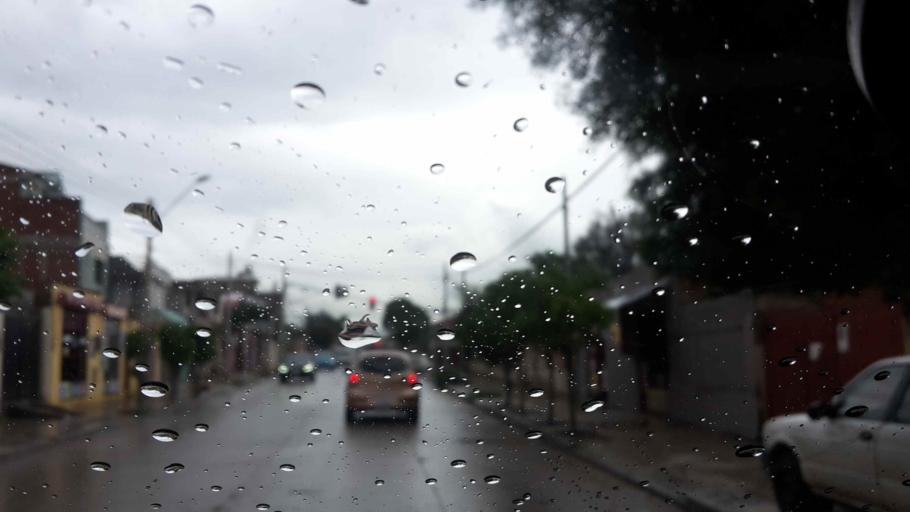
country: BO
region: Cochabamba
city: Cochabamba
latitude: -17.4137
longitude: -66.1489
